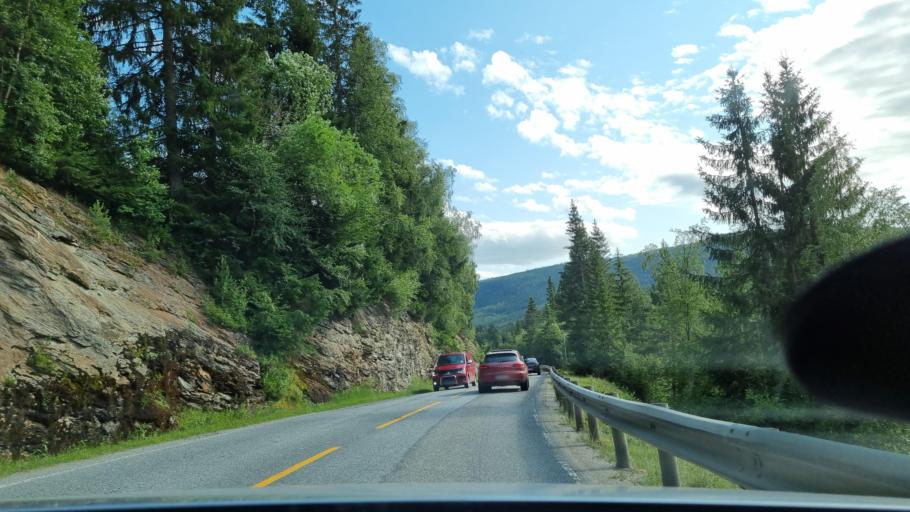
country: NO
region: Sor-Trondelag
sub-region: Holtalen
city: Alen
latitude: 62.8638
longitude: 11.2133
